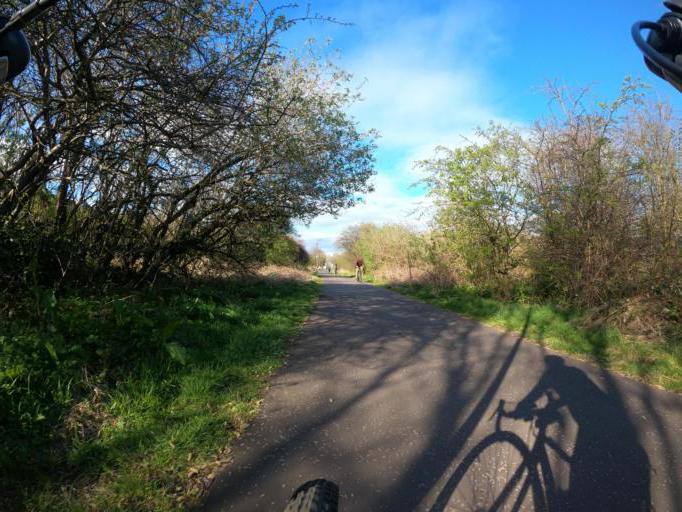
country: GB
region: Scotland
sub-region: Edinburgh
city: Edinburgh
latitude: 55.9645
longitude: -3.2418
